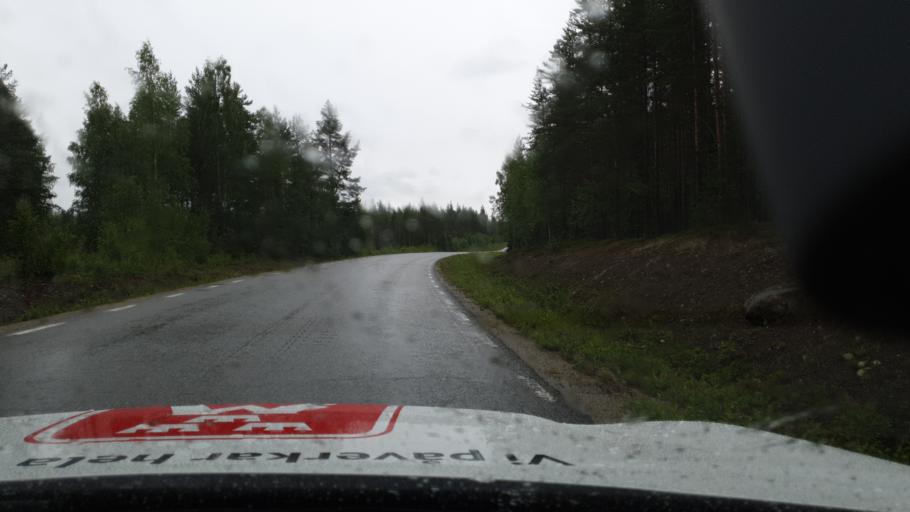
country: SE
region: Vaesterbotten
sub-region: Vindelns Kommun
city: Vindeln
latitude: 64.4128
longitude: 19.6690
